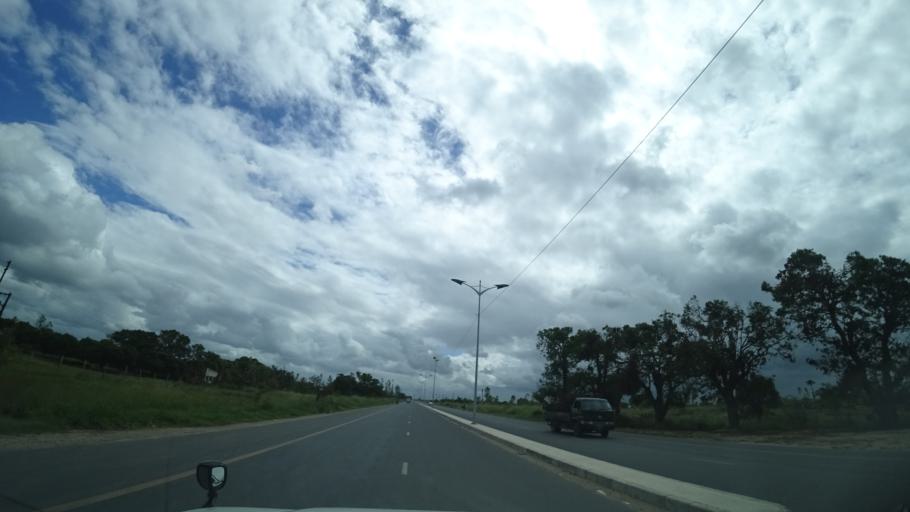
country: MZ
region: Sofala
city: Dondo
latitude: -19.5915
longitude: 34.7377
